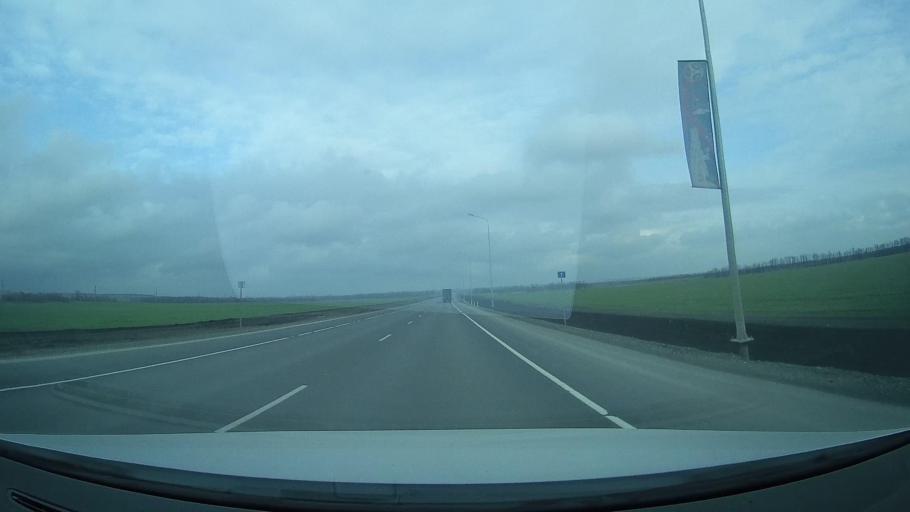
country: RU
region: Rostov
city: Grushevskaya
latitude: 47.4380
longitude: 39.8721
